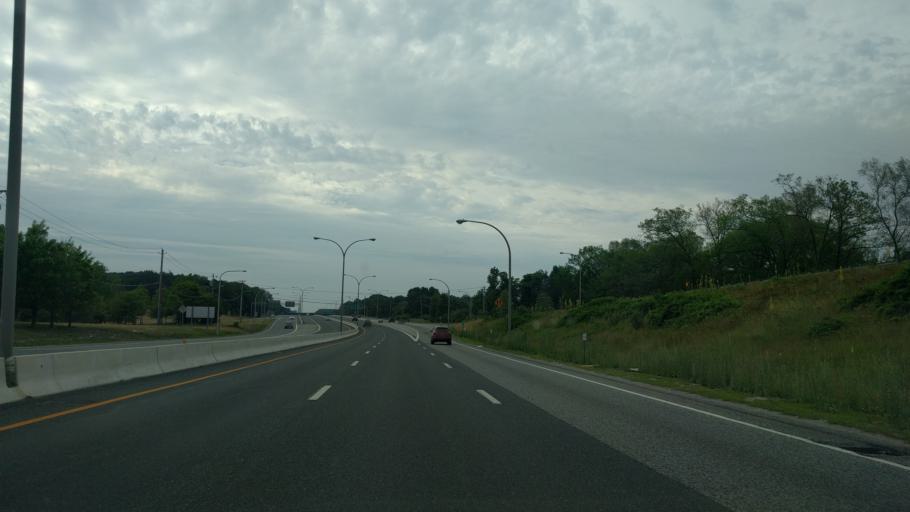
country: US
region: Rhode Island
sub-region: Providence County
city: Cumberland Hill
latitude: 41.9499
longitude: -71.4843
